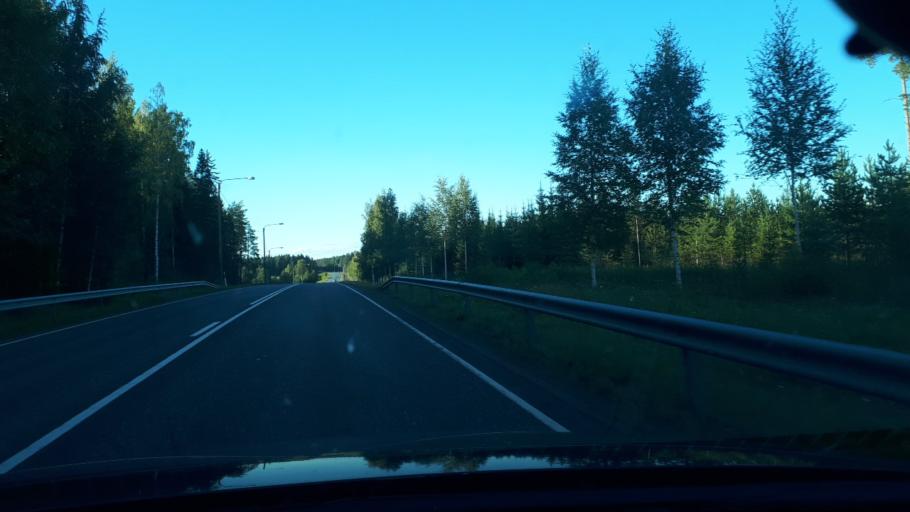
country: FI
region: Northern Savo
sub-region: Ylae-Savo
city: Lapinlahti
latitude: 63.4312
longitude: 27.3277
